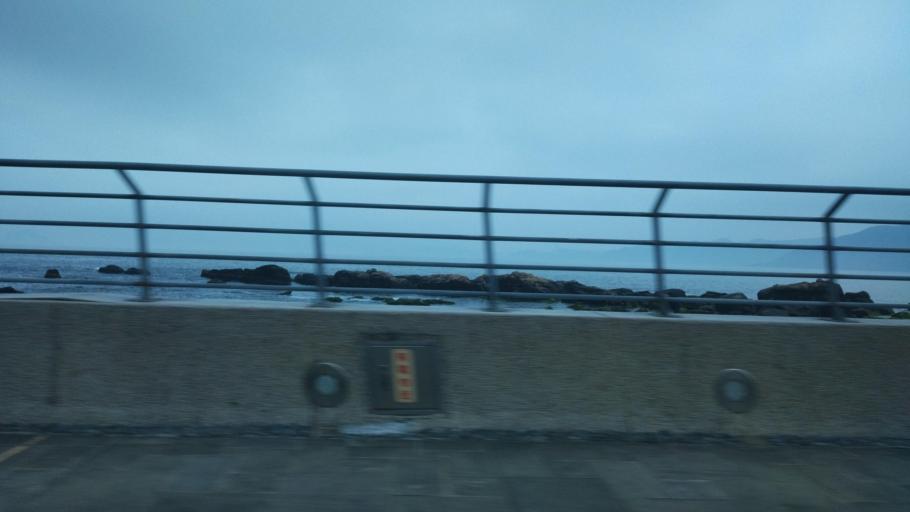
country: TW
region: Taiwan
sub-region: Keelung
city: Keelung
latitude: 25.2004
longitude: 121.6922
